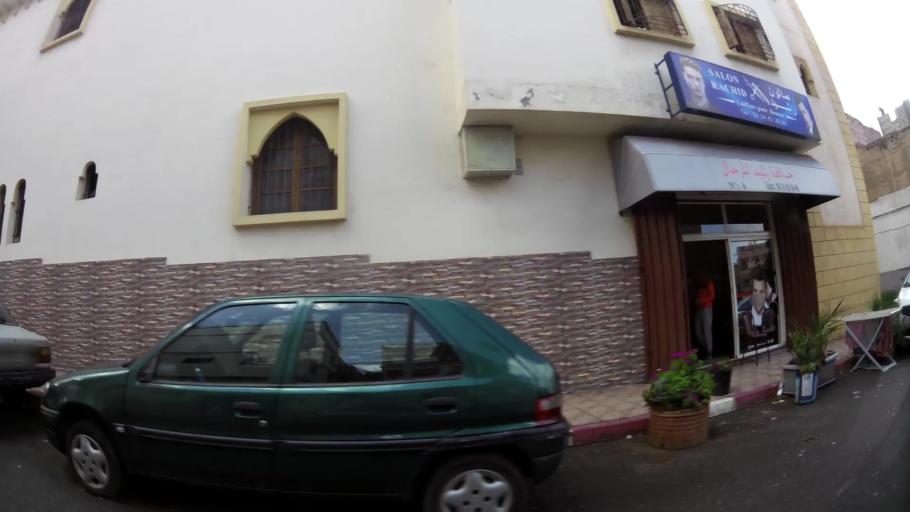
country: MA
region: Grand Casablanca
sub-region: Casablanca
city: Casablanca
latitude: 33.5490
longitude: -7.5977
